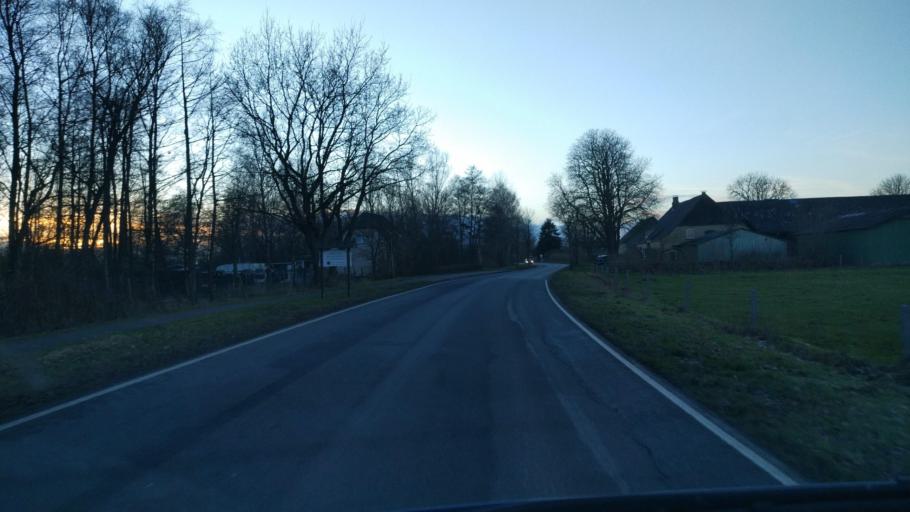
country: DE
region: Schleswig-Holstein
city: Dorpstedt
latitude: 54.4424
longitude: 9.3720
